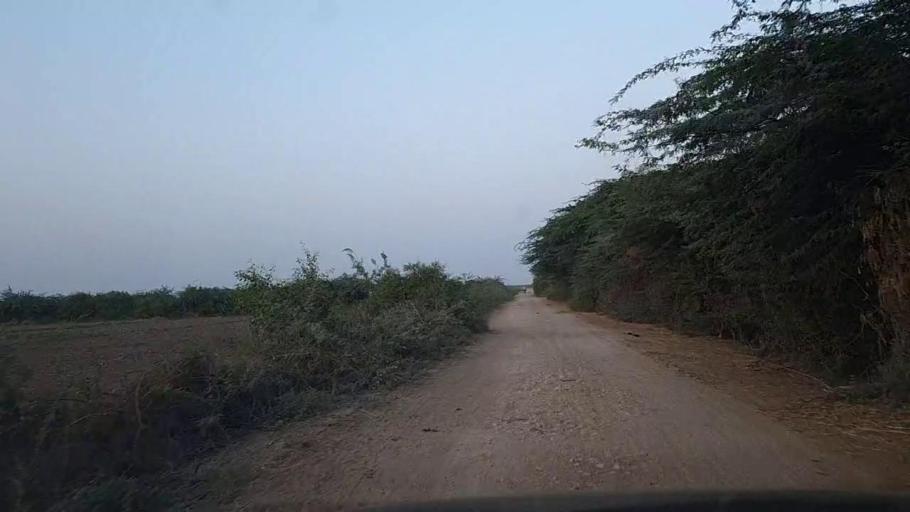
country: PK
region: Sindh
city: Mirpur Sakro
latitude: 24.6322
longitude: 67.6578
